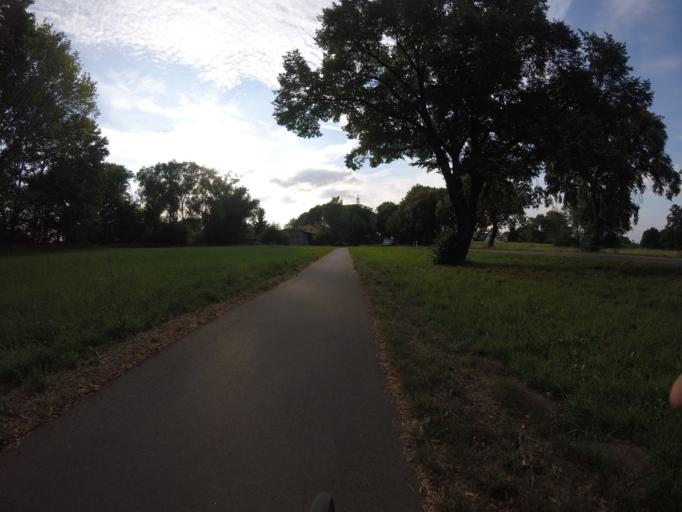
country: DE
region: Brandenburg
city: Altlandsberg
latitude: 52.5705
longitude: 13.7189
